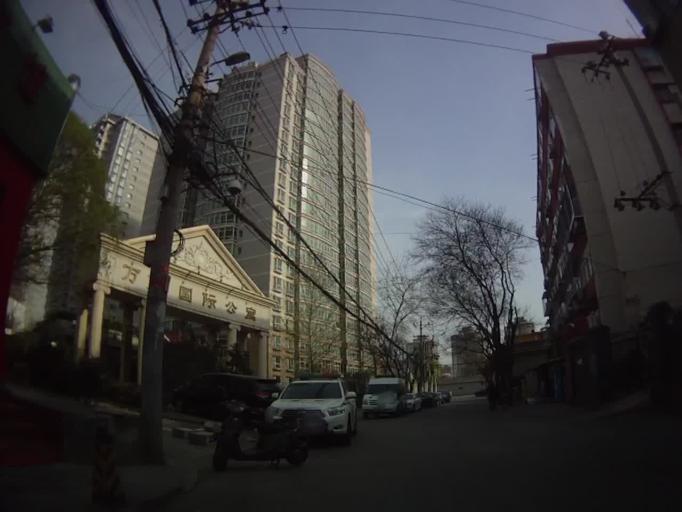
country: CN
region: Beijing
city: Chaowai
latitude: 39.9034
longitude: 116.4418
